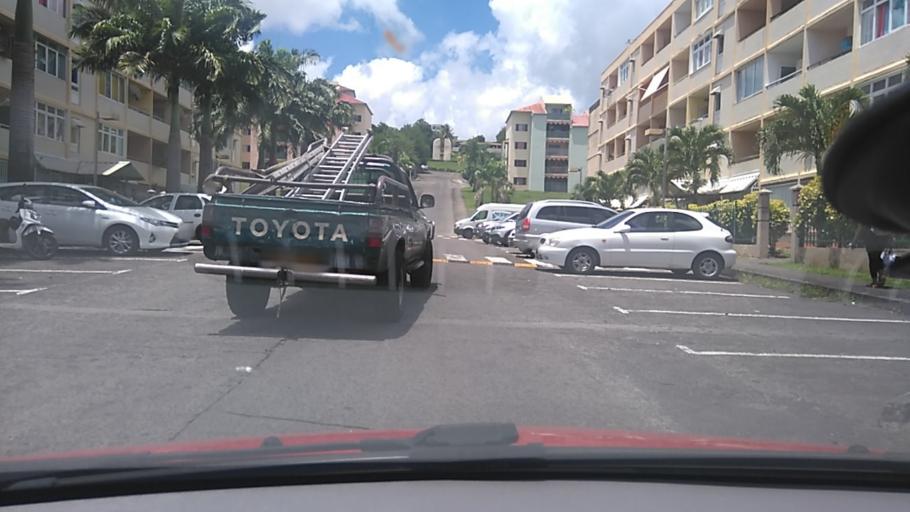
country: MQ
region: Martinique
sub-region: Martinique
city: Fort-de-France
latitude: 14.6103
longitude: -61.0454
